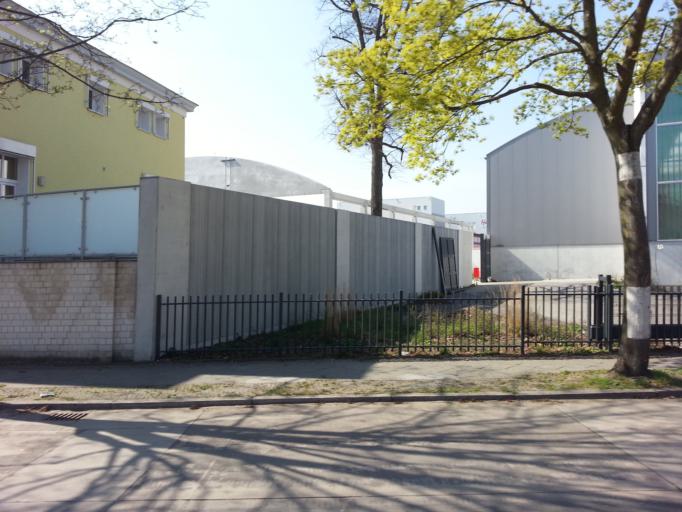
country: DE
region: Berlin
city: Charlottenburg-Nord
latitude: 52.5465
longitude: 13.3116
